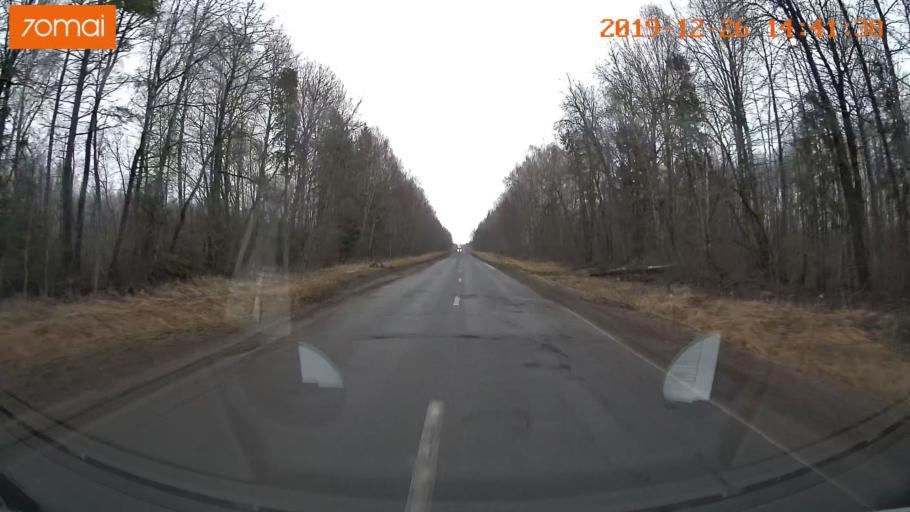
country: RU
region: Jaroslavl
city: Poshekhon'ye
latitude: 58.3696
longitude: 39.0217
